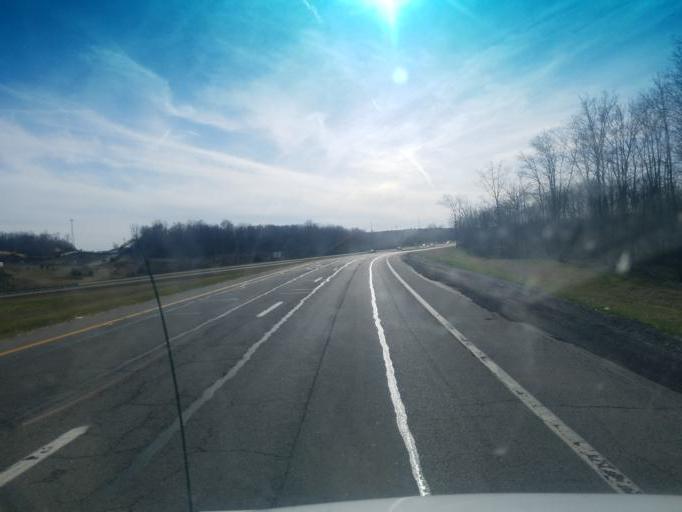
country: US
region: Ohio
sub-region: Champaign County
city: North Lewisburg
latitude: 40.3243
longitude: -83.5870
